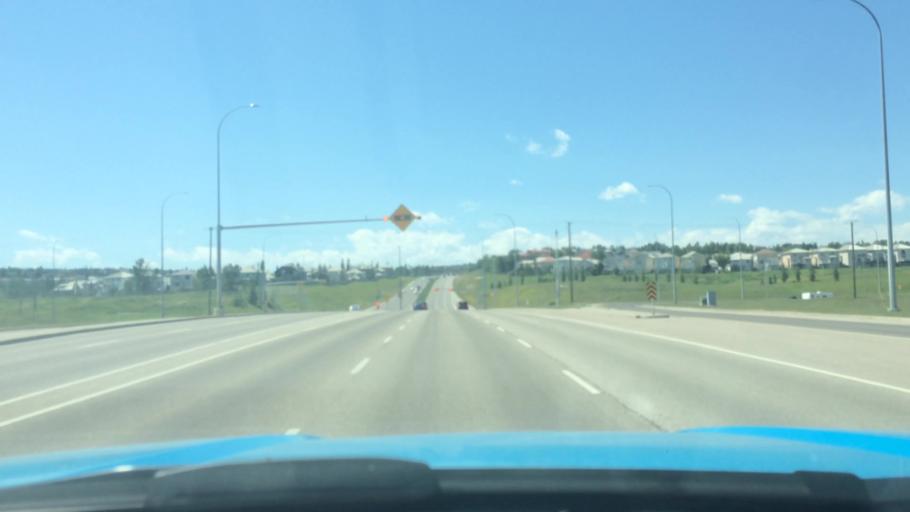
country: CA
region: Alberta
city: Calgary
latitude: 51.1435
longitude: -114.1214
